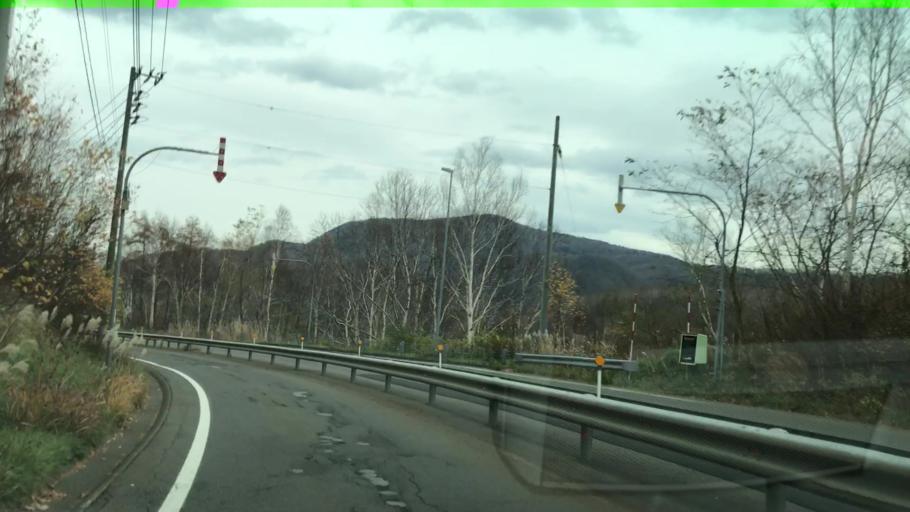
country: JP
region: Hokkaido
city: Yoichi
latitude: 43.2885
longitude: 140.5803
